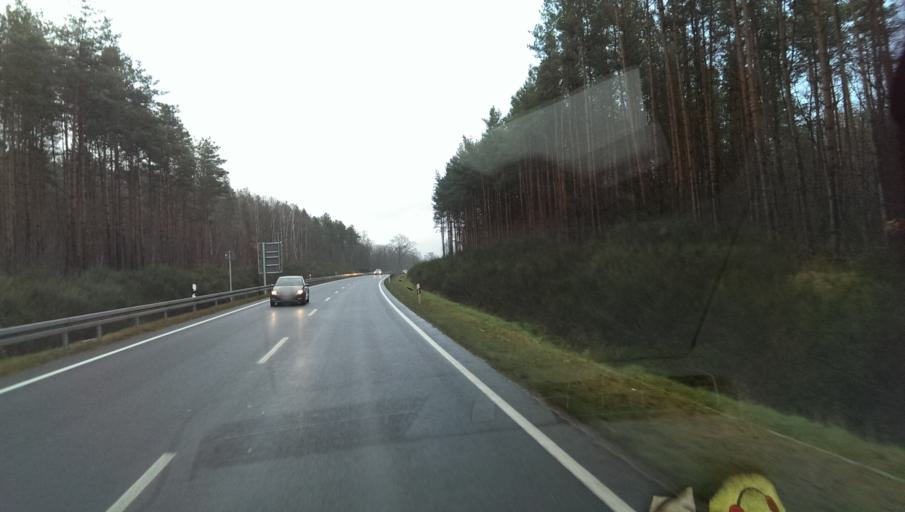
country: DE
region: Saxony
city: Moritzburg
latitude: 51.1579
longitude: 13.6353
